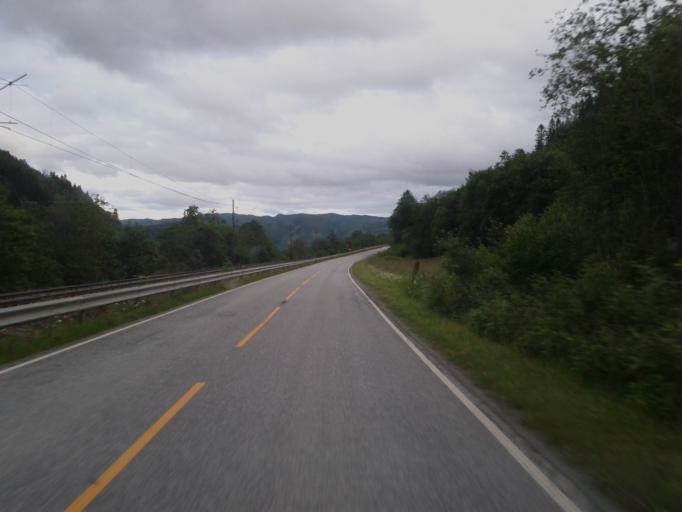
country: NO
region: Sor-Trondelag
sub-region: Midtre Gauldal
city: Storen
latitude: 63.0623
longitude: 10.2881
